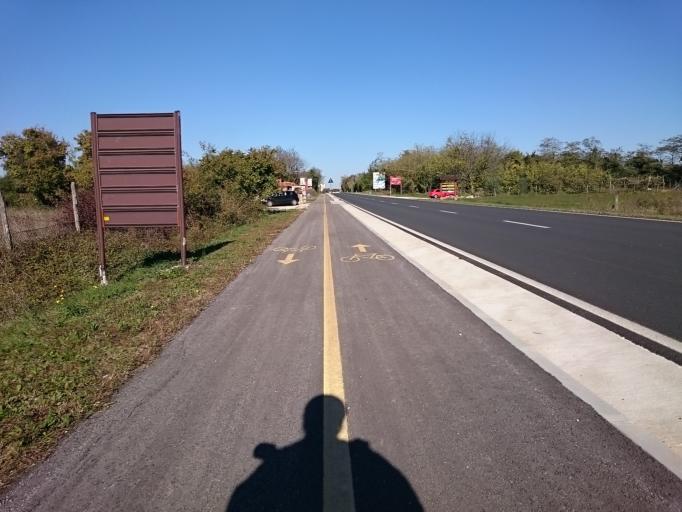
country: HR
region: Istarska
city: Umag
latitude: 45.4226
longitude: 13.5309
